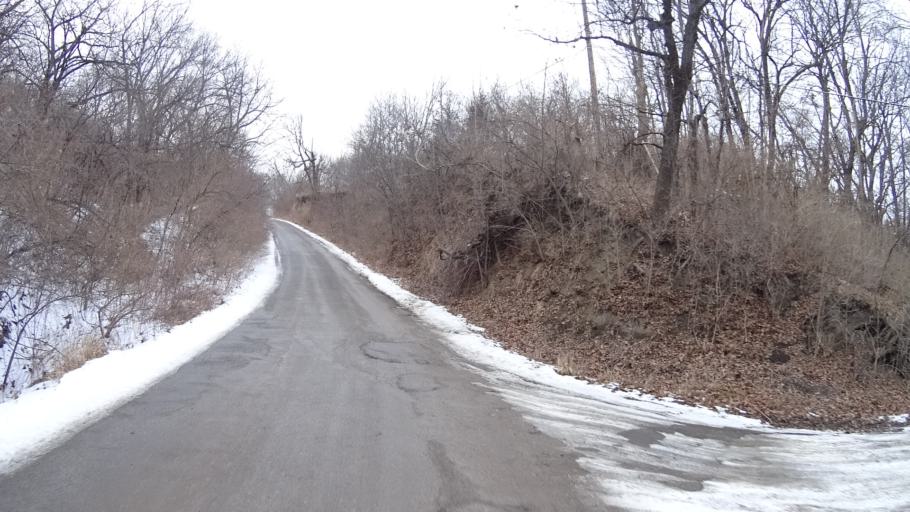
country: US
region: Nebraska
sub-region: Sarpy County
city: Bellevue
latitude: 41.1731
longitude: -95.9072
